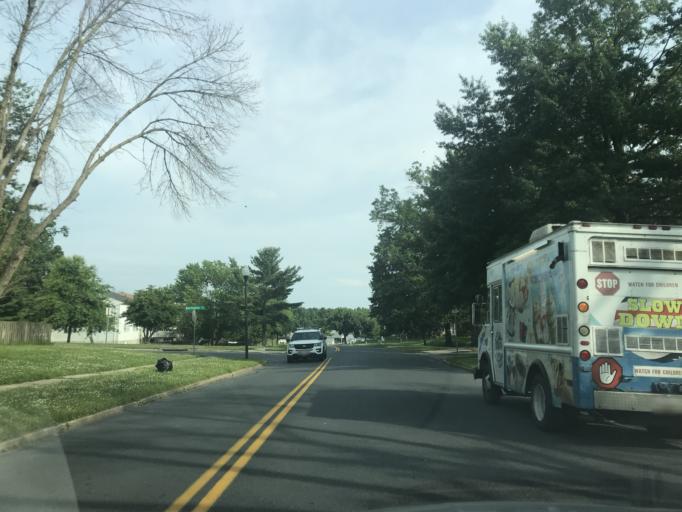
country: US
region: Maryland
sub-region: Harford County
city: Edgewood
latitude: 39.4220
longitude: -76.3219
